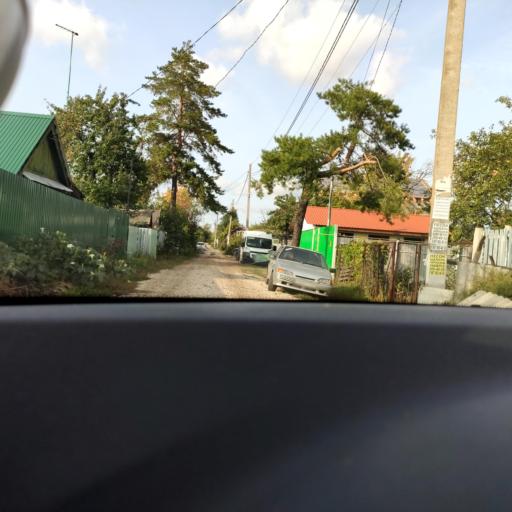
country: RU
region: Samara
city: Petra-Dubrava
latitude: 53.2762
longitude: 50.2969
